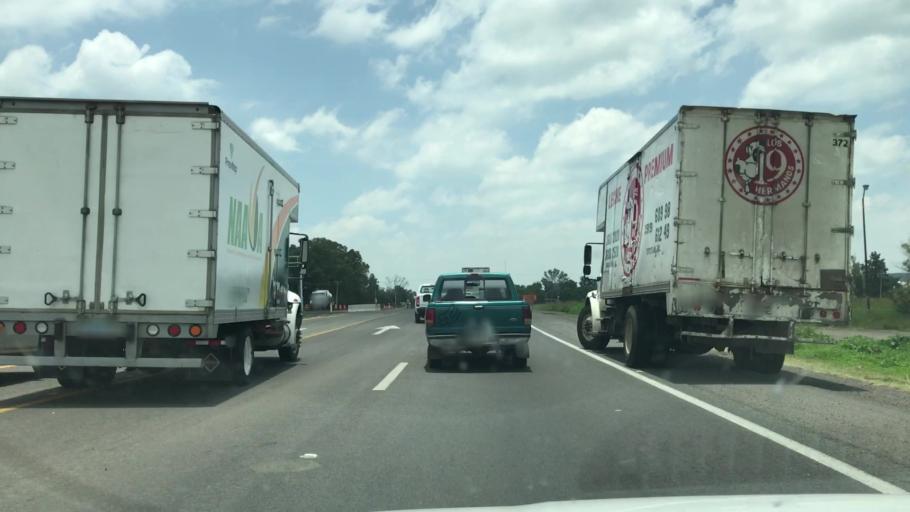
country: MX
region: Guanajuato
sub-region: Irapuato
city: San Ignacio de Rivera (Ojo de Agua)
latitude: 20.5323
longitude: -101.4596
